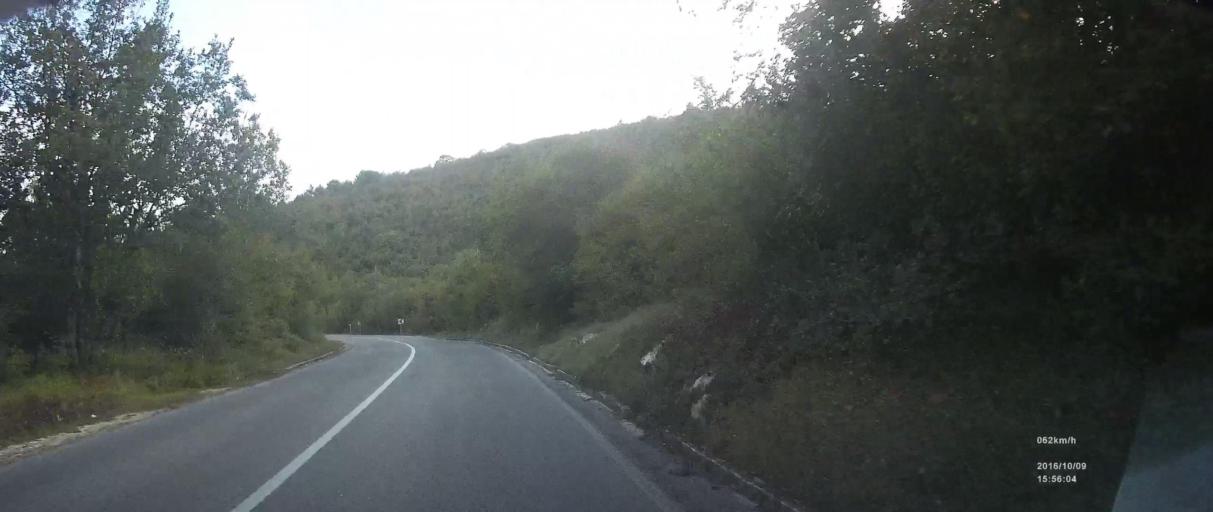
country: HR
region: Splitsko-Dalmatinska
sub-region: Grad Trogir
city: Trogir
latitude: 43.5811
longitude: 16.2317
